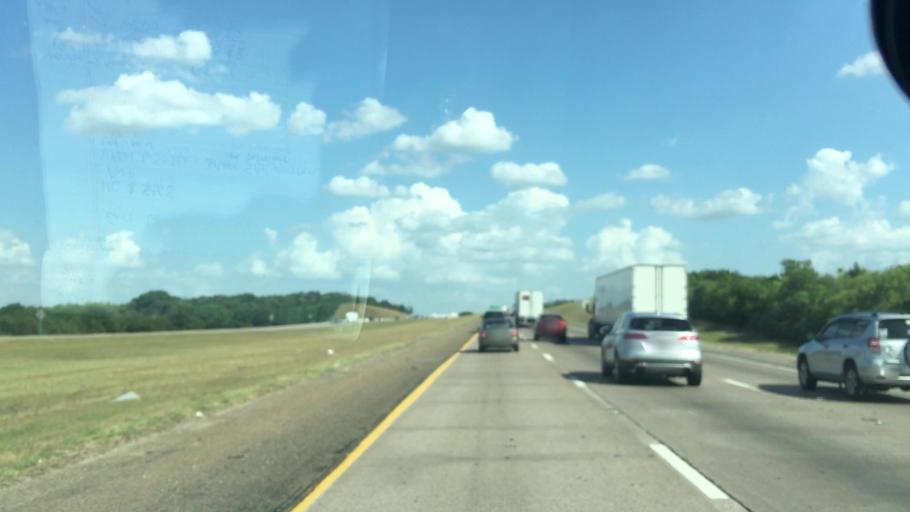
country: US
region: Texas
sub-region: Dallas County
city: Hutchins
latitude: 32.6737
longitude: -96.7376
